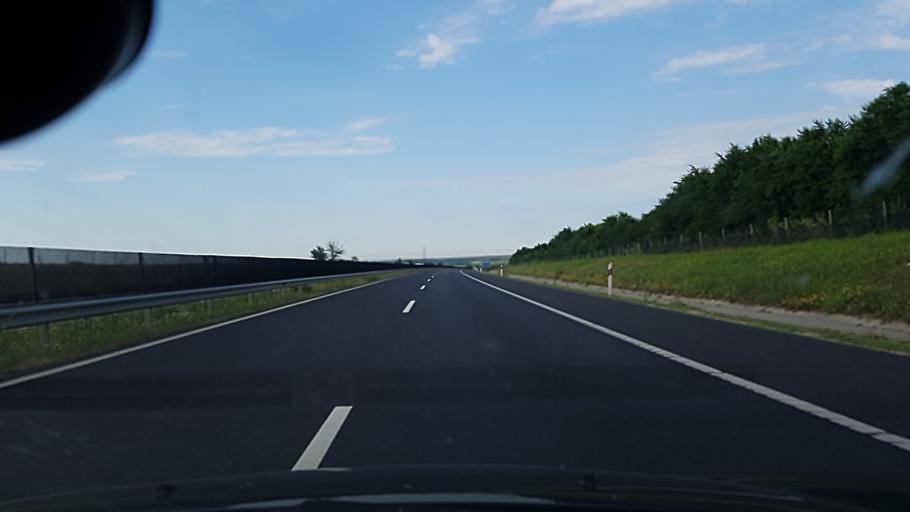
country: HU
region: Fejer
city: Rackeresztur
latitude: 47.2780
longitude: 18.8613
